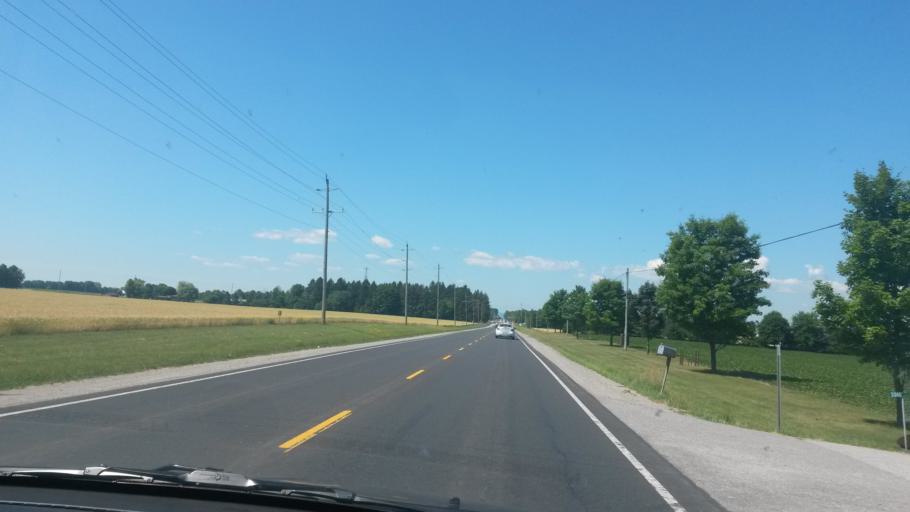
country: CA
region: Ontario
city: Barrie
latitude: 44.5031
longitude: -79.7837
